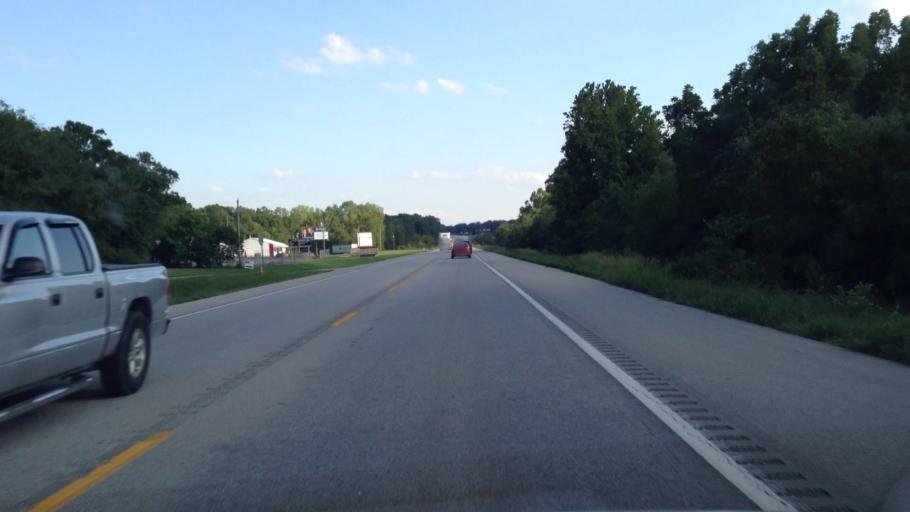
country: US
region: Missouri
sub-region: Jasper County
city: Carl Junction
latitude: 37.1537
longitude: -94.5265
